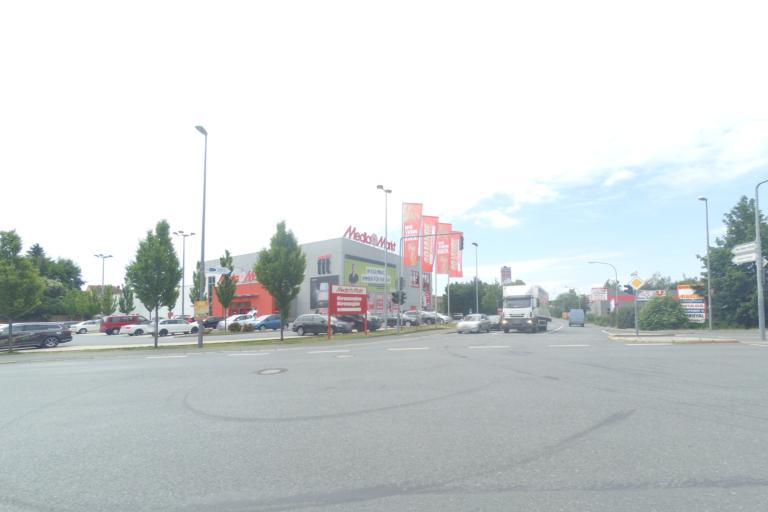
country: DE
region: Bavaria
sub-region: Upper Franconia
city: Kulmbach
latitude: 50.1130
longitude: 11.4465
